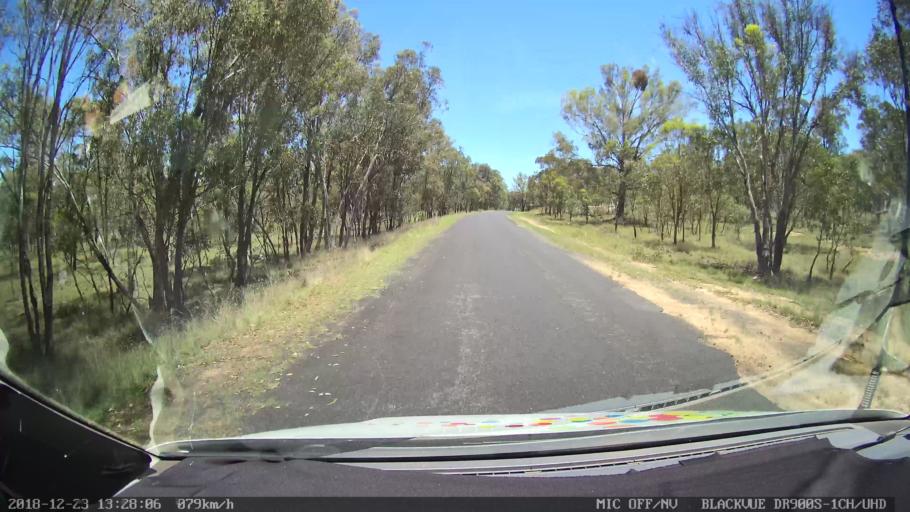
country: AU
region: New South Wales
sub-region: Armidale Dumaresq
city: Armidale
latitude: -30.4642
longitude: 151.3523
